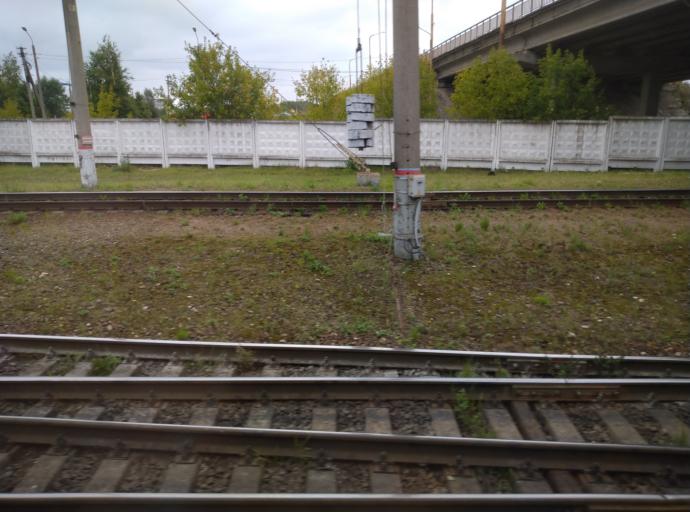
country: RU
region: Kostroma
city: Oktyabr'skiy
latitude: 57.7558
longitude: 40.9796
